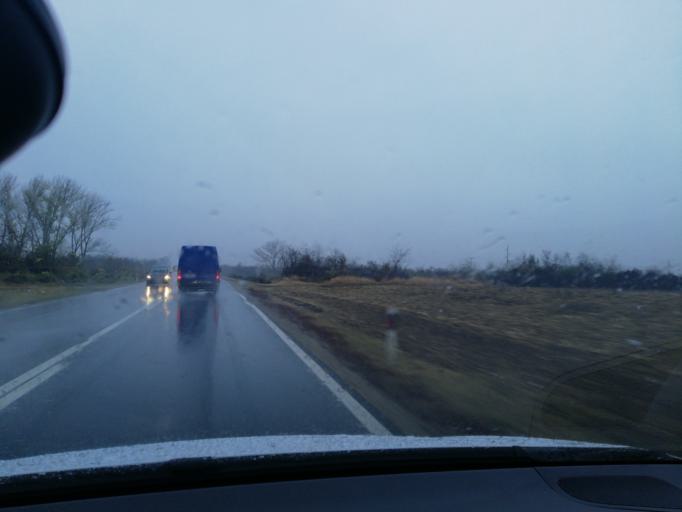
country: RS
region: Autonomna Pokrajina Vojvodina
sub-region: Sremski Okrug
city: Ruma
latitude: 45.0221
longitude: 19.8365
